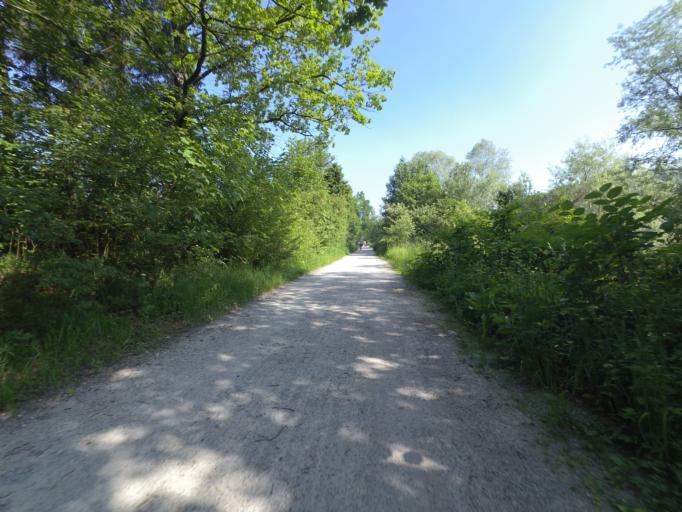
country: AT
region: Salzburg
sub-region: Politischer Bezirk Salzburg-Umgebung
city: Elsbethen
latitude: 47.7590
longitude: 13.0768
